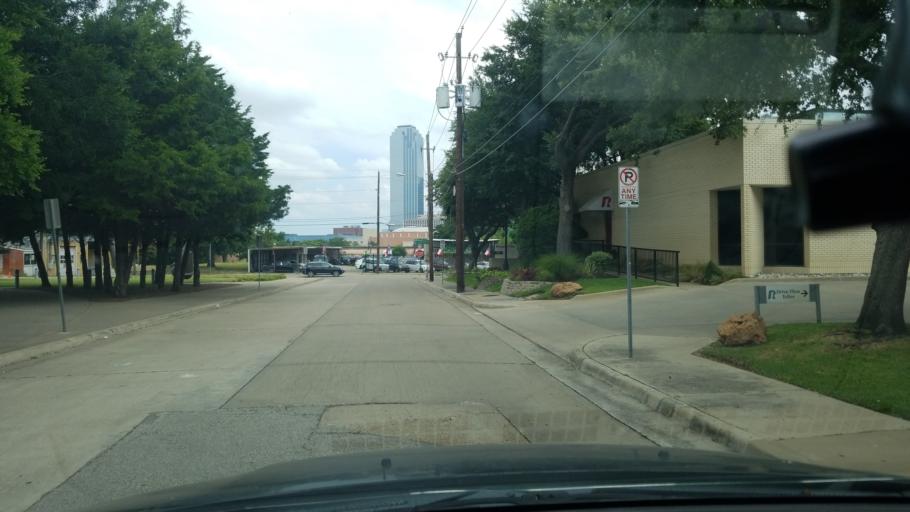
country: US
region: Texas
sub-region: Dallas County
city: Dallas
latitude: 32.7692
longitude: -96.7932
